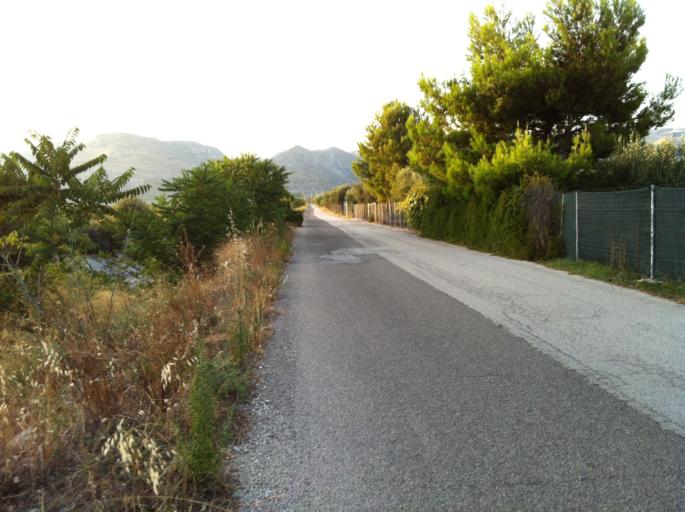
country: IT
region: Apulia
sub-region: Provincia di Foggia
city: Manfredonia
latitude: 41.6550
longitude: 15.9522
